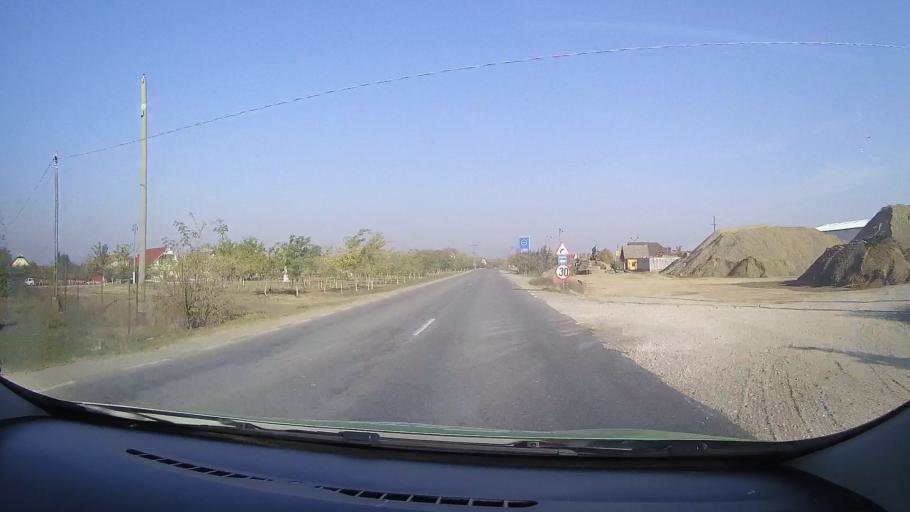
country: RO
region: Arad
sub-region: Comuna Pilu
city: Pilu
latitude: 46.5693
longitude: 21.3430
